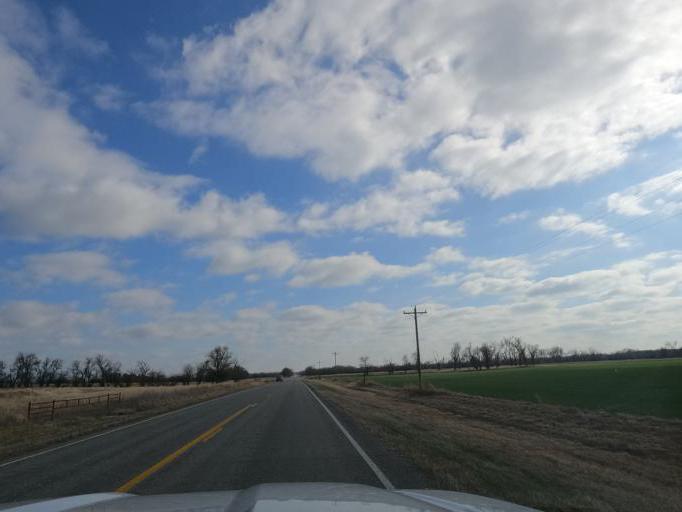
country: US
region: Kansas
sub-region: Reno County
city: Buhler
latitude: 38.1801
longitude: -97.8486
